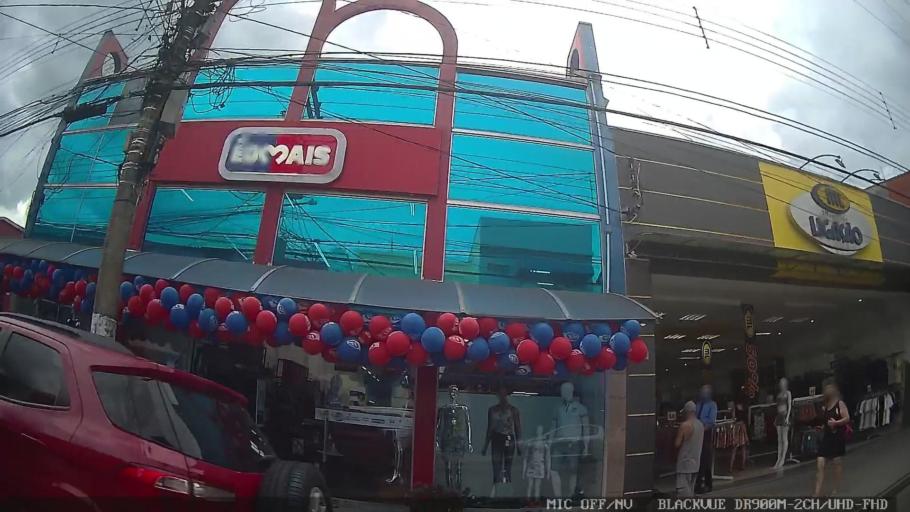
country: BR
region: Sao Paulo
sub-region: Atibaia
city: Atibaia
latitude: -23.1145
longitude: -46.5523
